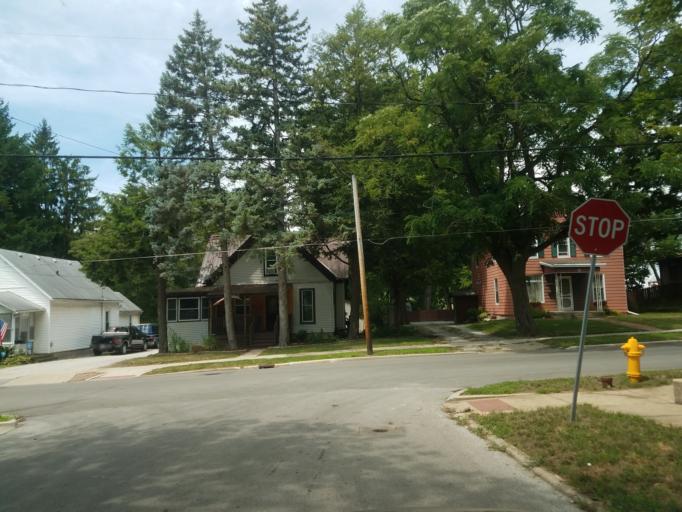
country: US
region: Illinois
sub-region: McLean County
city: Bloomington
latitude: 40.4712
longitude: -88.9854
